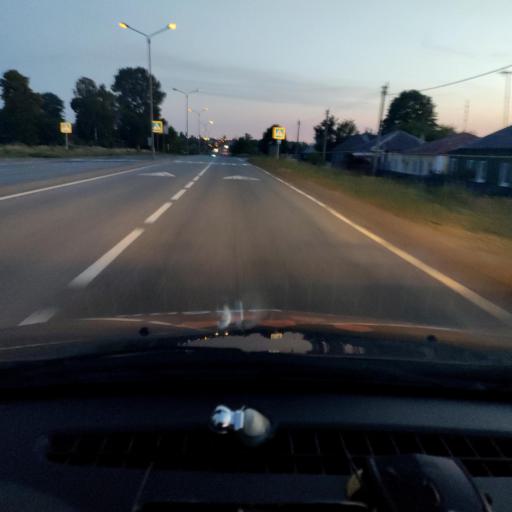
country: RU
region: Belgorod
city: Gubkin
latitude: 51.2768
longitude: 37.5921
